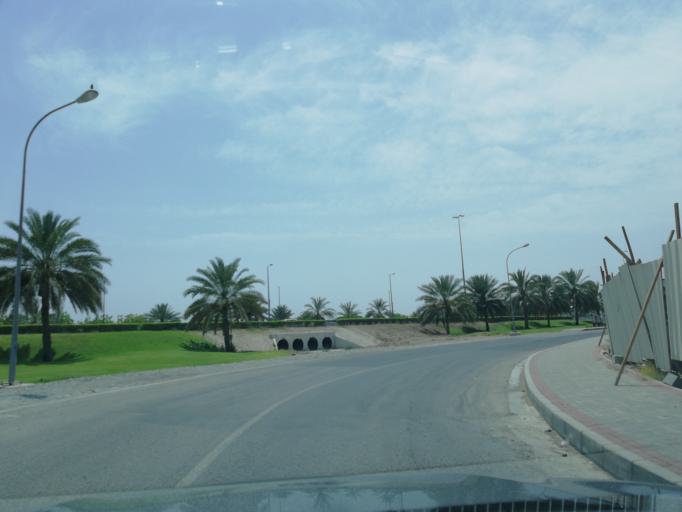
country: OM
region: Muhafazat Masqat
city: As Sib al Jadidah
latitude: 23.6575
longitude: 58.1971
